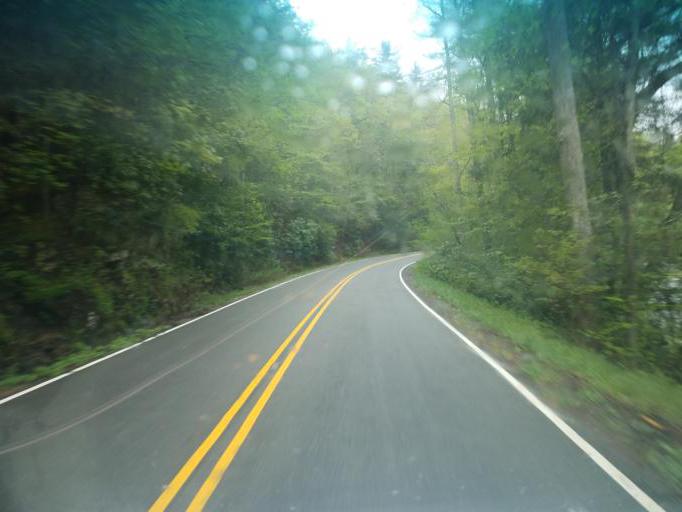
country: US
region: Tennessee
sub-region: Johnson County
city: Mountain City
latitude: 36.6280
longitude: -81.7567
